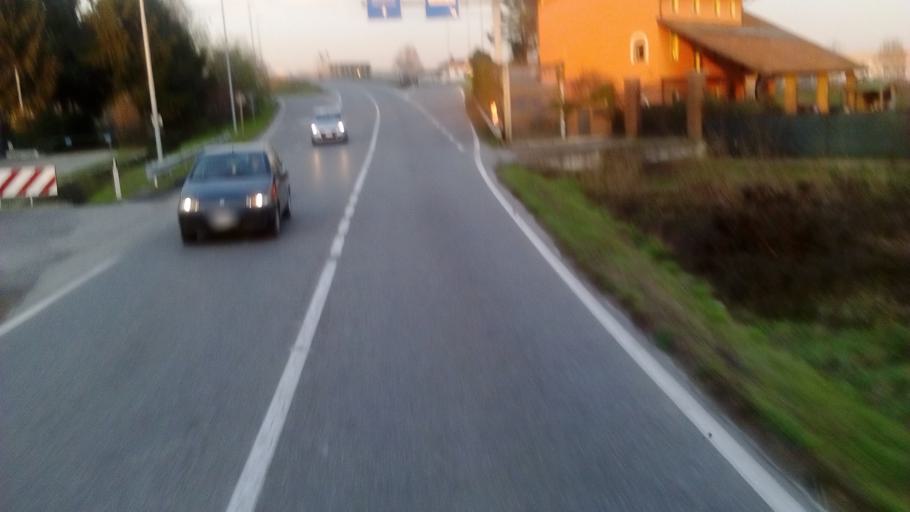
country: IT
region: Lombardy
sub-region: Provincia di Cremona
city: Soncino
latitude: 45.3895
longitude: 9.8541
